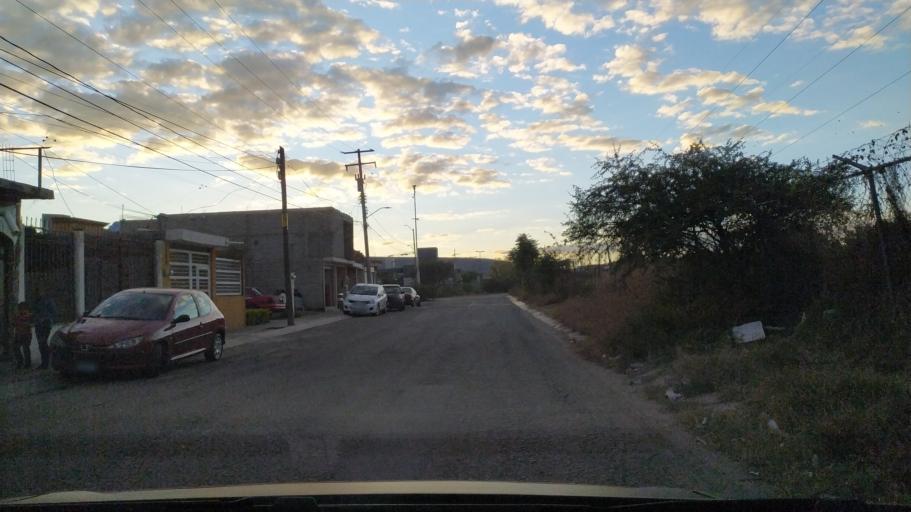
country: MX
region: Guanajuato
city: San Francisco del Rincon
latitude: 21.0385
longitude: -101.8483
